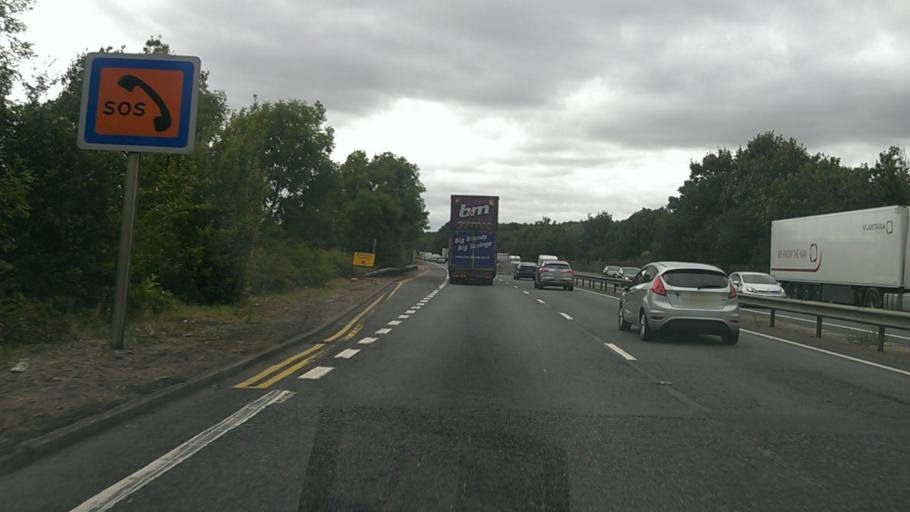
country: GB
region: England
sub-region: Cambridgeshire
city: Huntingdon
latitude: 52.3342
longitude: -0.1967
